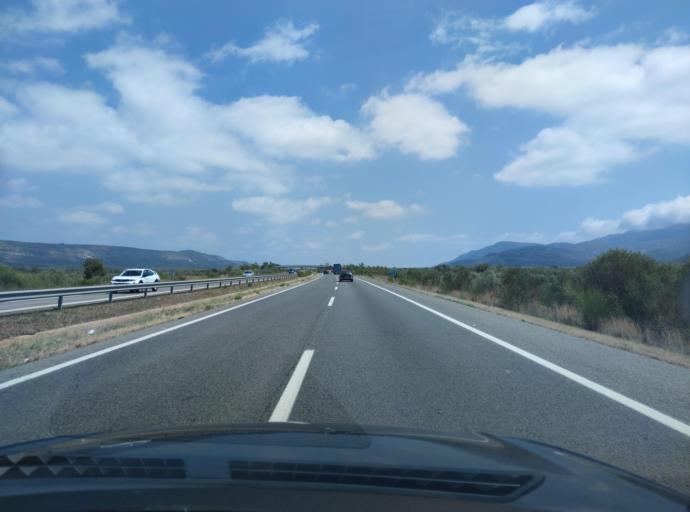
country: ES
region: Catalonia
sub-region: Provincia de Tarragona
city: Ulldecona
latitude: 40.5954
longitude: 0.4691
